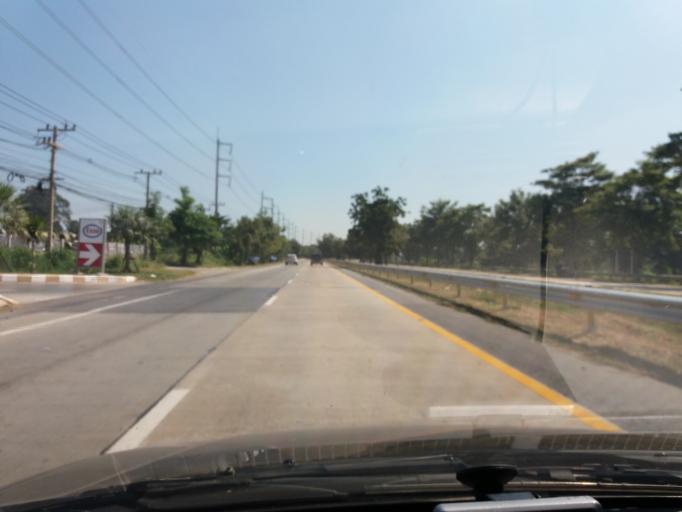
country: TH
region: Chai Nat
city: Chai Nat
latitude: 15.1428
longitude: 100.1410
